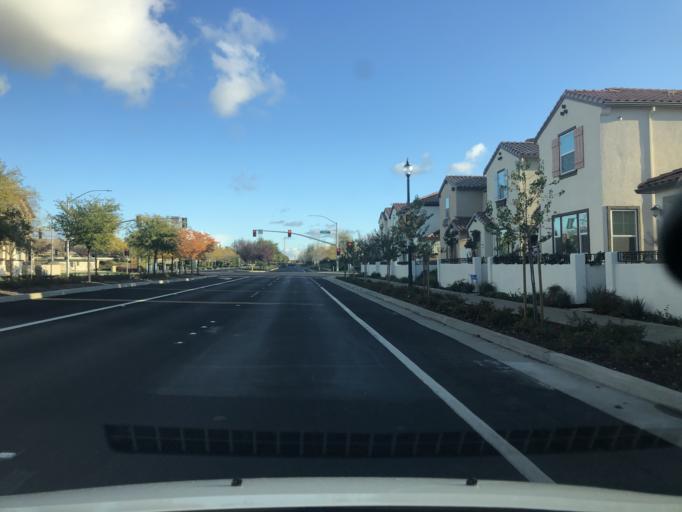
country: US
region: California
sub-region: Sacramento County
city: Antelope
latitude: 38.7703
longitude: -121.3676
